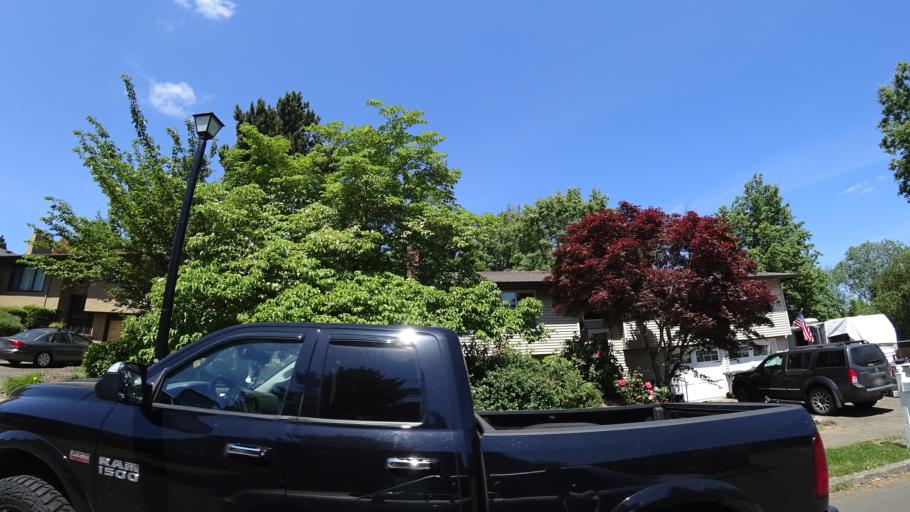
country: US
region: Oregon
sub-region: Washington County
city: King City
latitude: 45.4329
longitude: -122.8031
